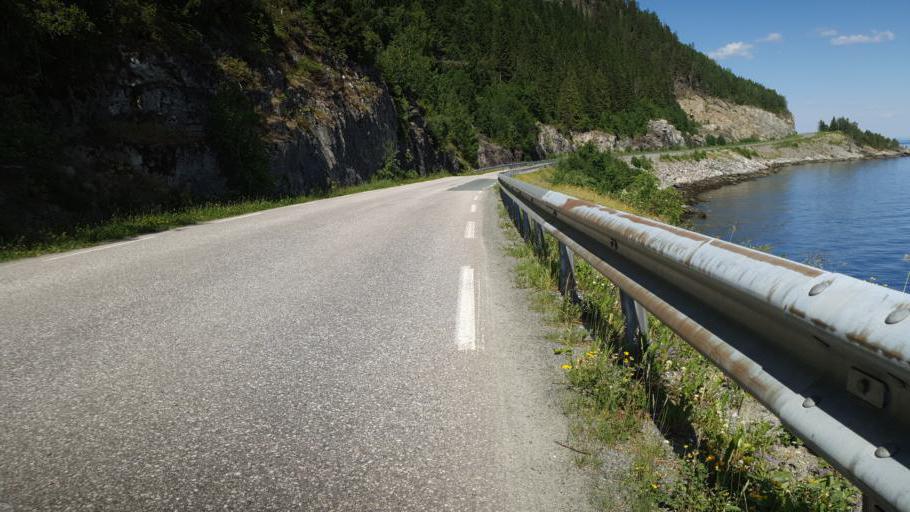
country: NO
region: Nord-Trondelag
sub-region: Leksvik
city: Leksvik
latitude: 63.6077
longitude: 10.4927
